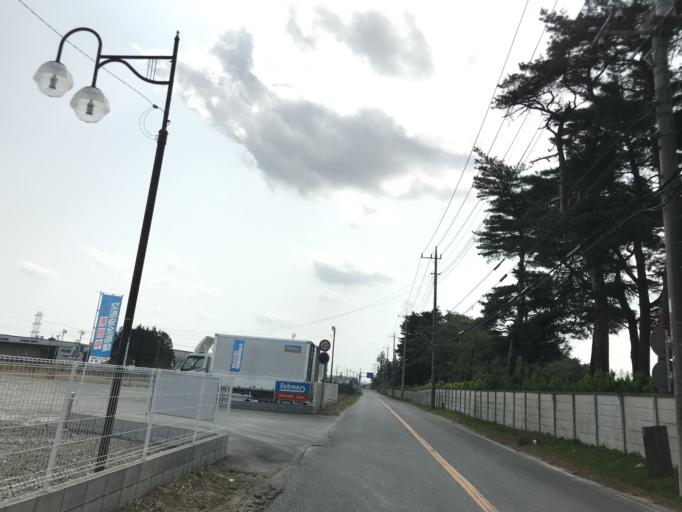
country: JP
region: Ibaraki
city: Ushiku
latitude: 35.9977
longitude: 140.0682
